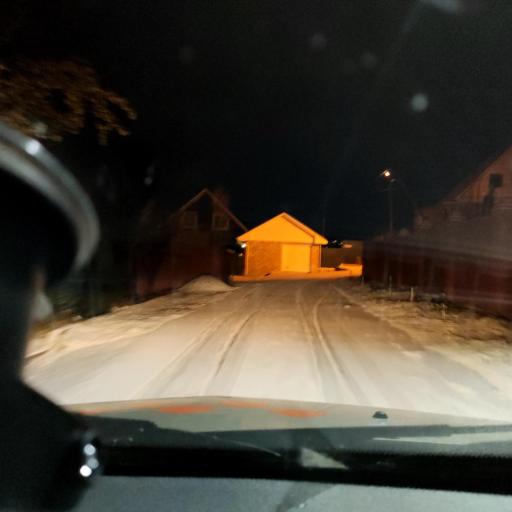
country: RU
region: Bashkortostan
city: Mikhaylovka
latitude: 54.8270
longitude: 55.9118
